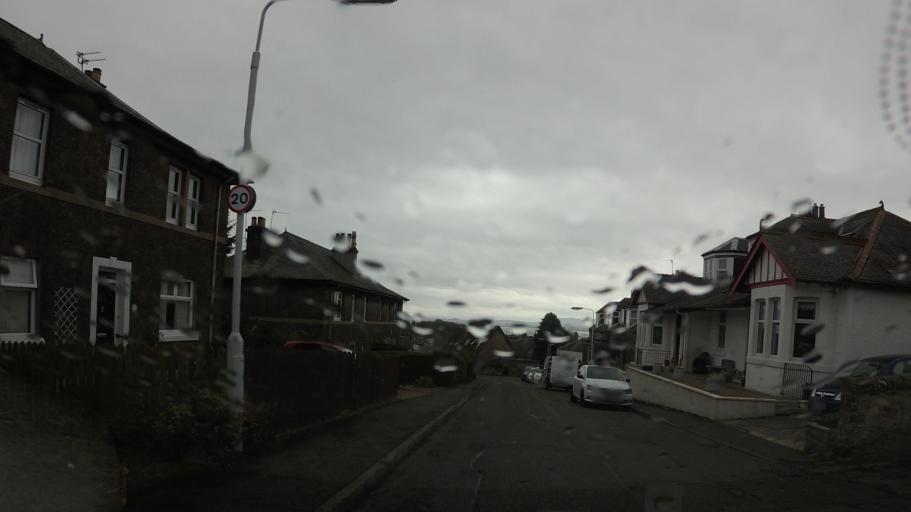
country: GB
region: Scotland
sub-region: Fife
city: Aberdour
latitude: 56.0583
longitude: -3.2968
